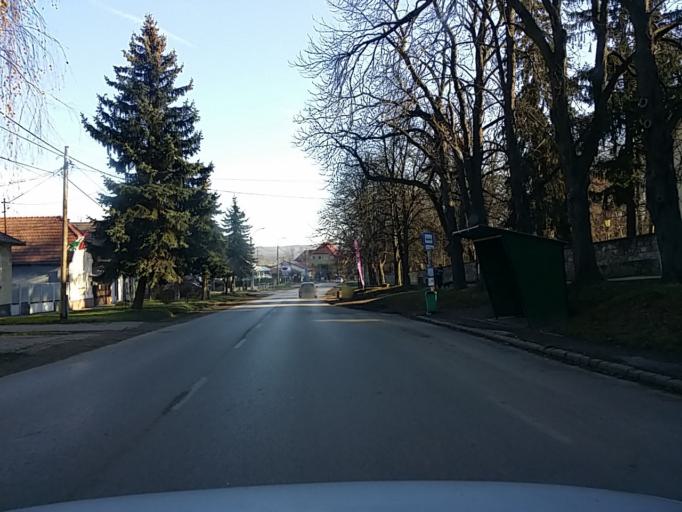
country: HU
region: Pest
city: Pilisszentivan
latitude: 47.5760
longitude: 18.8908
